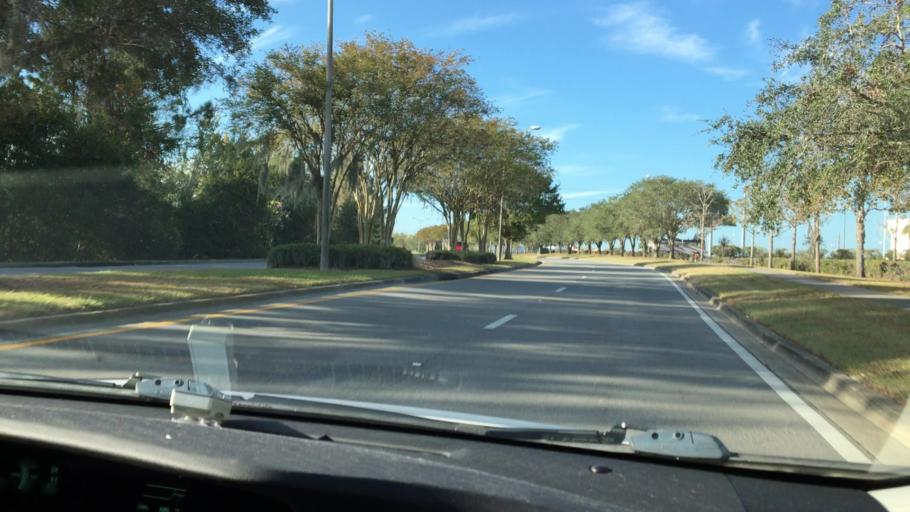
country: US
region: Florida
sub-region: Seminole County
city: Lake Mary
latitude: 28.8026
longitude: -81.3371
